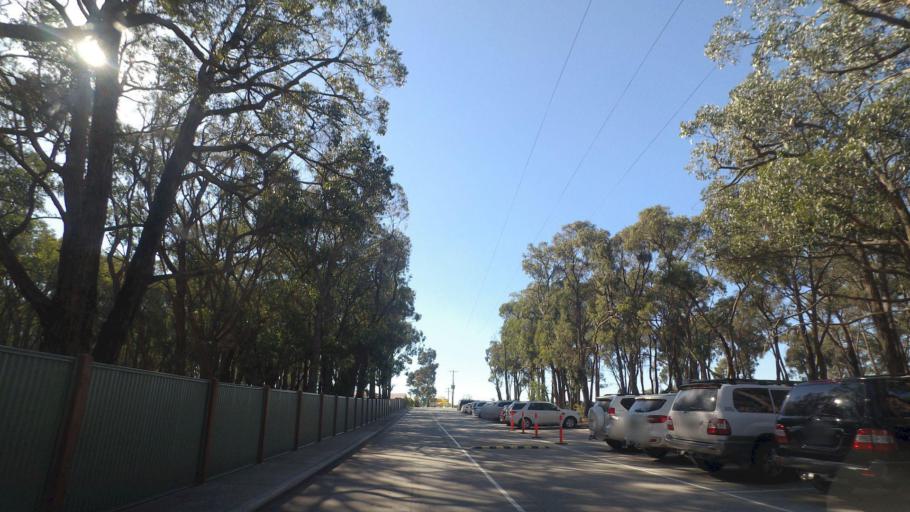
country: AU
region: Victoria
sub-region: Cardinia
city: Garfield
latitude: -38.0703
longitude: 145.6556
